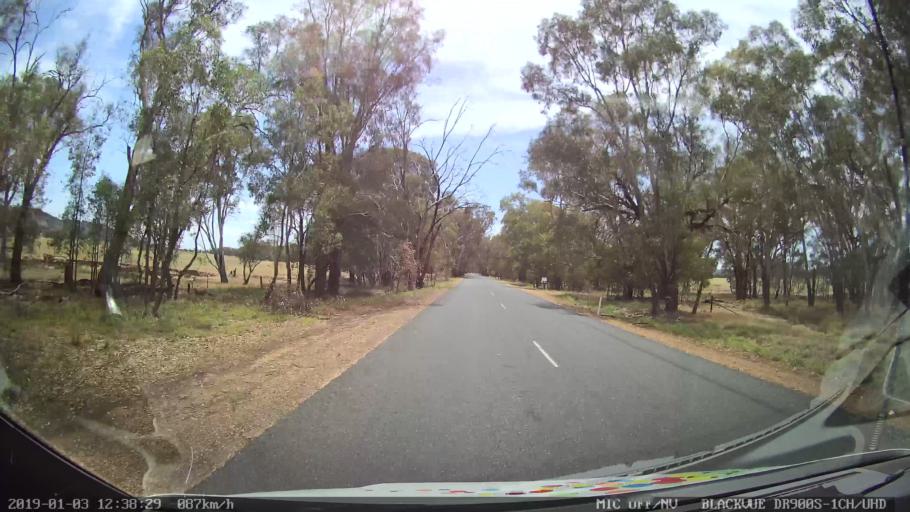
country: AU
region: New South Wales
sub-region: Weddin
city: Grenfell
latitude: -33.8330
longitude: 148.1962
